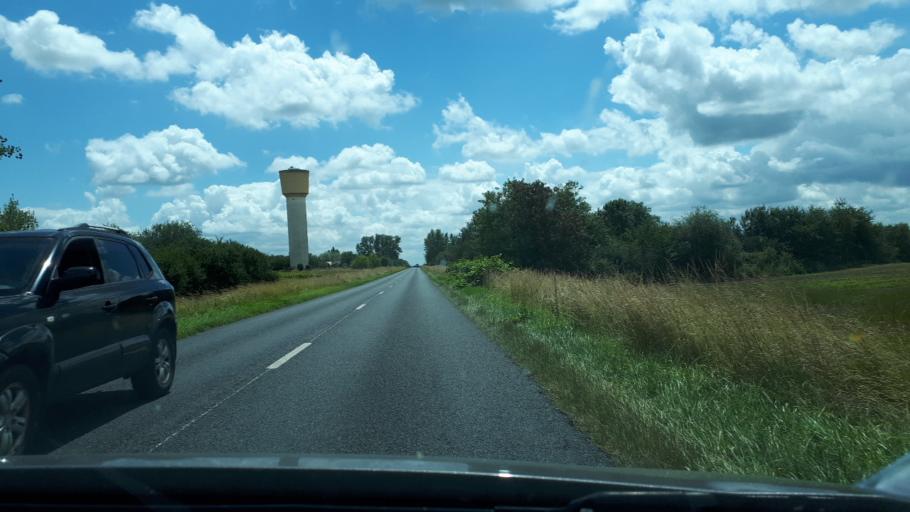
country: FR
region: Centre
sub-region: Departement du Loir-et-Cher
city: Contres
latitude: 47.3907
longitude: 1.4086
